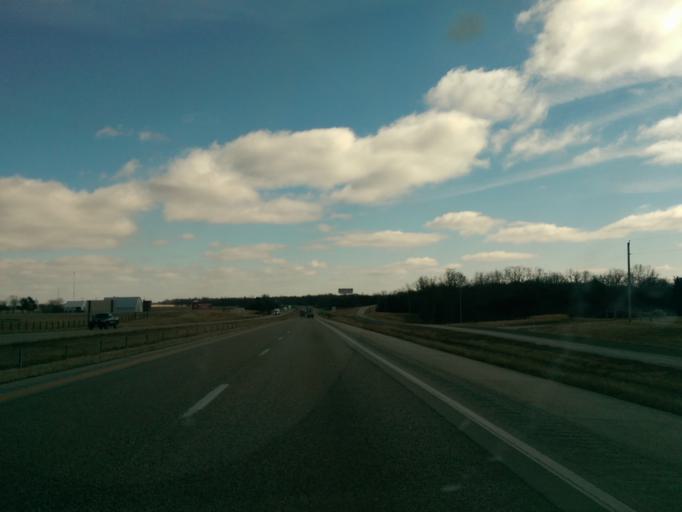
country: US
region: Missouri
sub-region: Montgomery County
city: Montgomery City
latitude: 38.8707
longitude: -91.3653
